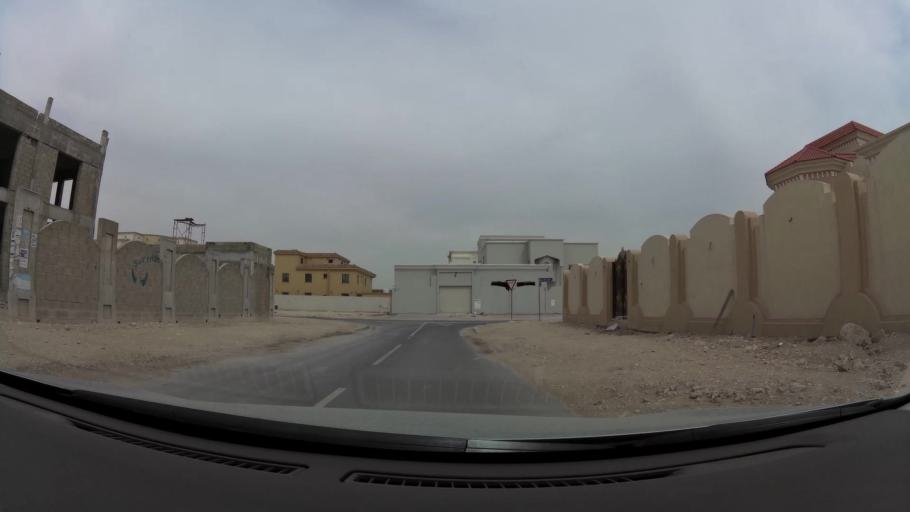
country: QA
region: Baladiyat ar Rayyan
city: Ar Rayyan
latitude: 25.2119
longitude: 51.4497
